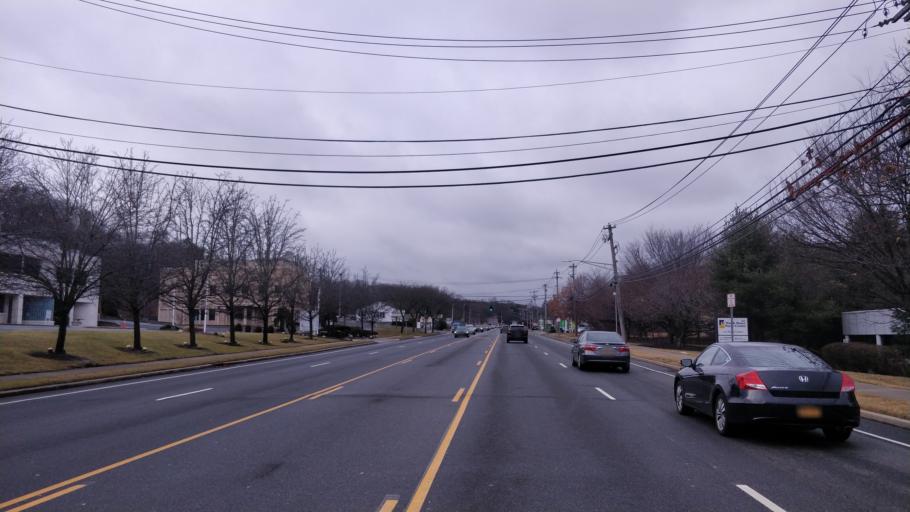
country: US
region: New York
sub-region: Suffolk County
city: Kings Park
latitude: 40.8480
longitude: -73.2498
